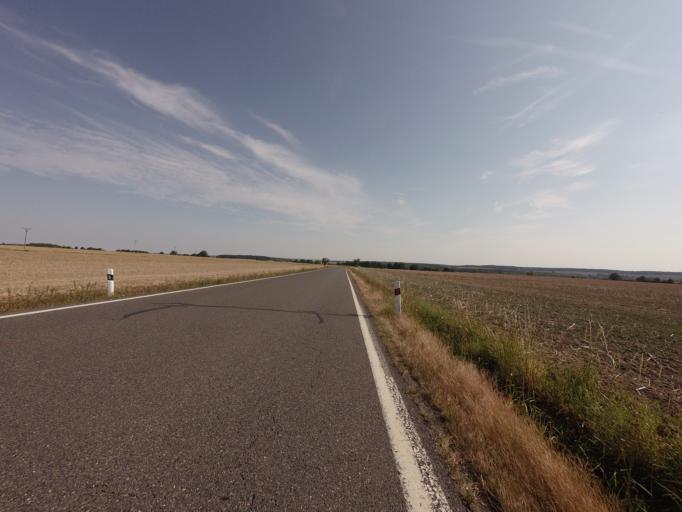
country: CZ
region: Jihocesky
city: Bernartice
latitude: 49.3345
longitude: 14.3623
